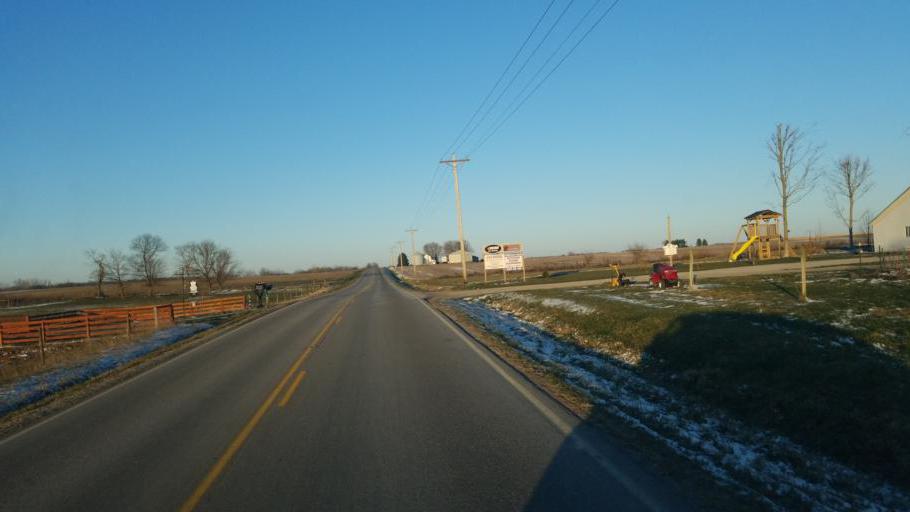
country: US
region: Ohio
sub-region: Highland County
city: Leesburg
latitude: 39.2642
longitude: -83.5106
